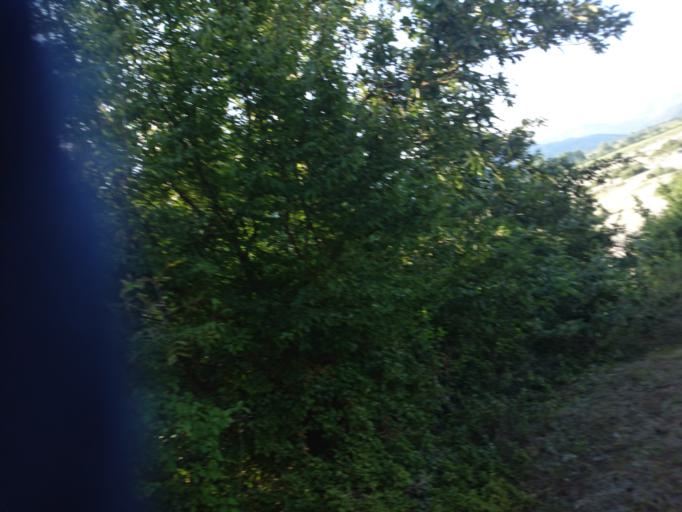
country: AL
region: Diber
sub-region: Rrethi i Dibres
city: Arras
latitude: 41.7376
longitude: 20.3310
